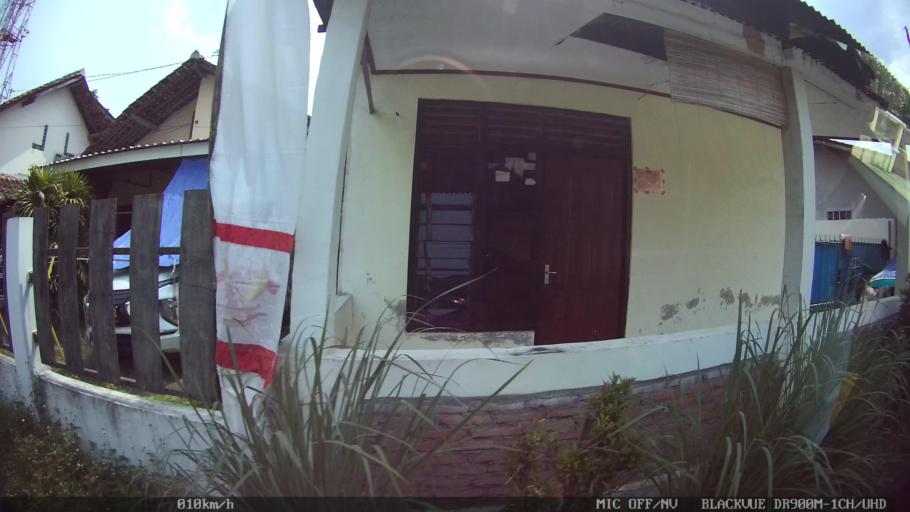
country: ID
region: Daerah Istimewa Yogyakarta
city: Depok
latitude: -7.7962
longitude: 110.4033
